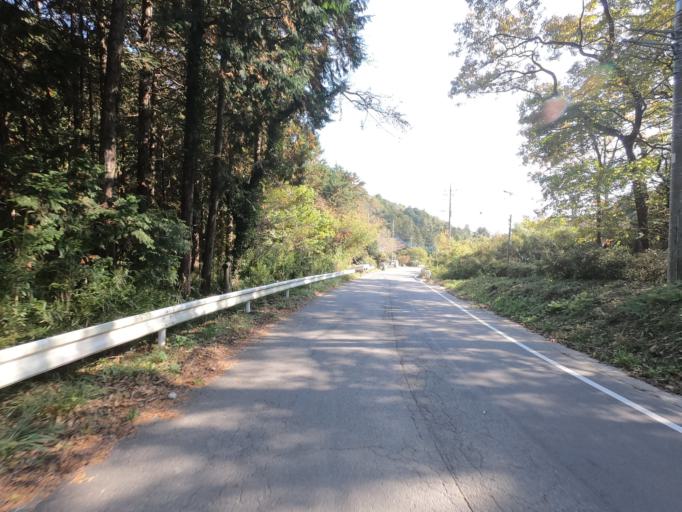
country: JP
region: Ibaraki
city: Makabe
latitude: 36.2355
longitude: 140.1321
